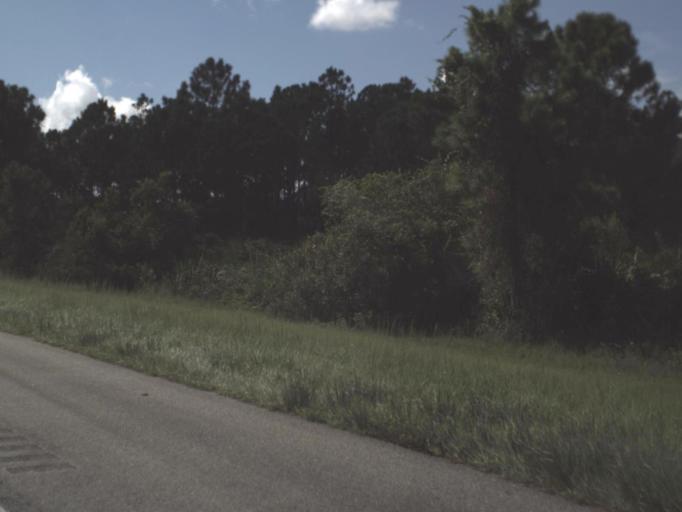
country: US
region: Florida
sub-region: Lee County
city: Suncoast Estates
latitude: 26.7848
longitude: -81.9008
